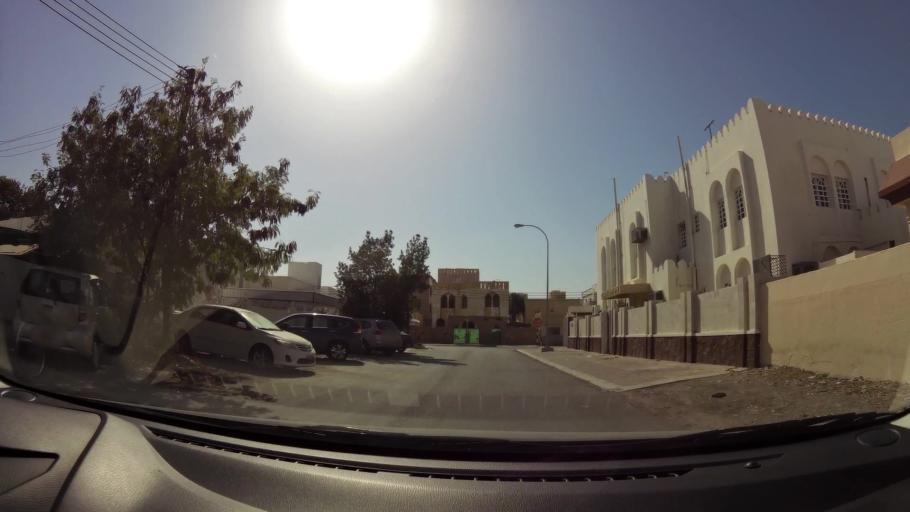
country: OM
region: Muhafazat Masqat
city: As Sib al Jadidah
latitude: 23.6283
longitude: 58.2010
